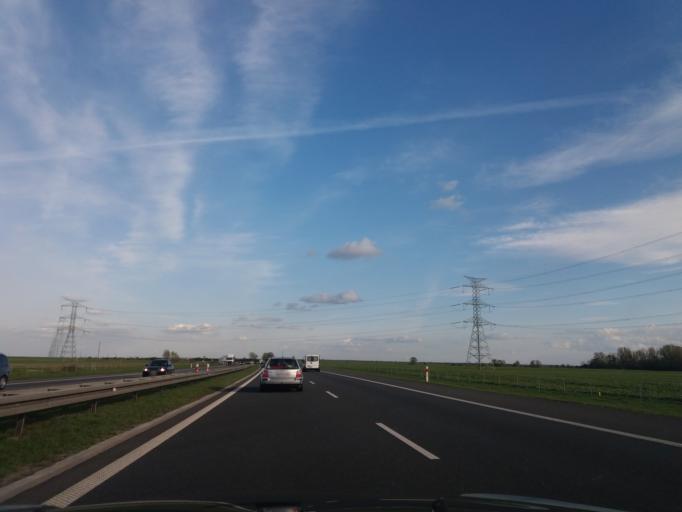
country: PL
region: Opole Voivodeship
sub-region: Powiat brzeski
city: Olszanka
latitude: 50.7437
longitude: 17.4548
